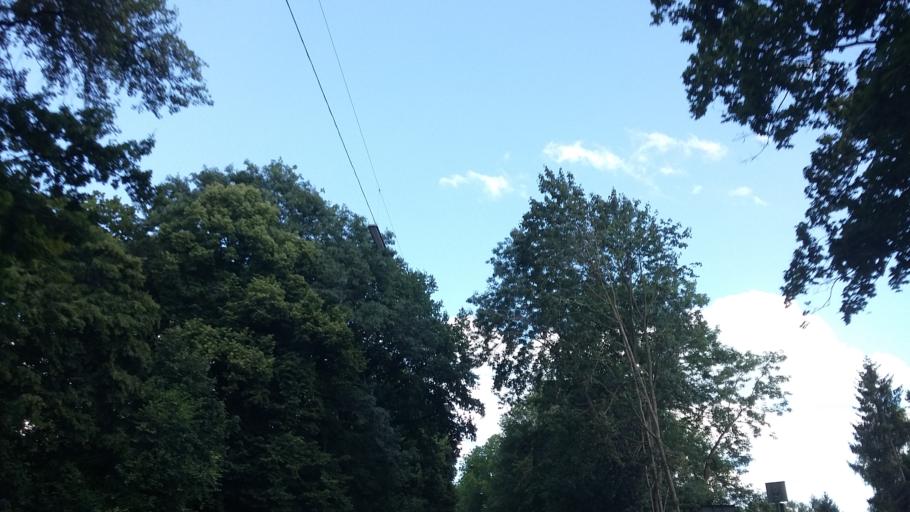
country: DE
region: Bavaria
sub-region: Swabia
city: Augsburg
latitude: 48.3787
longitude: 10.9069
